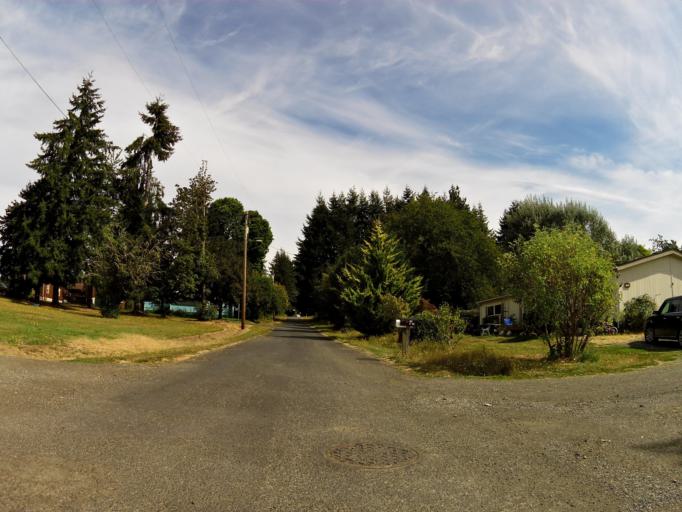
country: US
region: Washington
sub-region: Lewis County
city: Winlock
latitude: 46.4008
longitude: -122.9585
